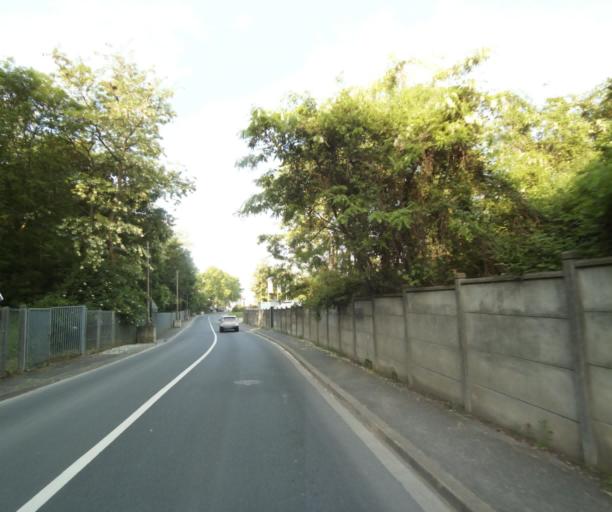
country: FR
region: Ile-de-France
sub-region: Departement du Val-d'Oise
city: Sannois
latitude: 48.9601
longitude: 2.2635
